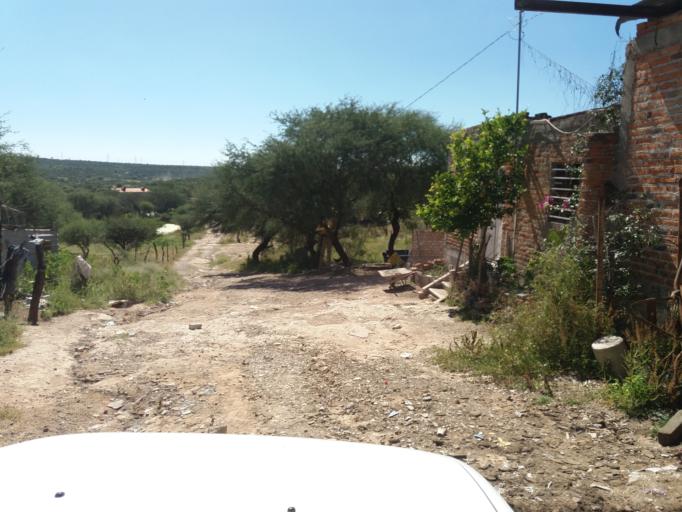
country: MX
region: Aguascalientes
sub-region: Aguascalientes
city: San Sebastian [Fraccionamiento]
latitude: 21.7757
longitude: -102.2282
